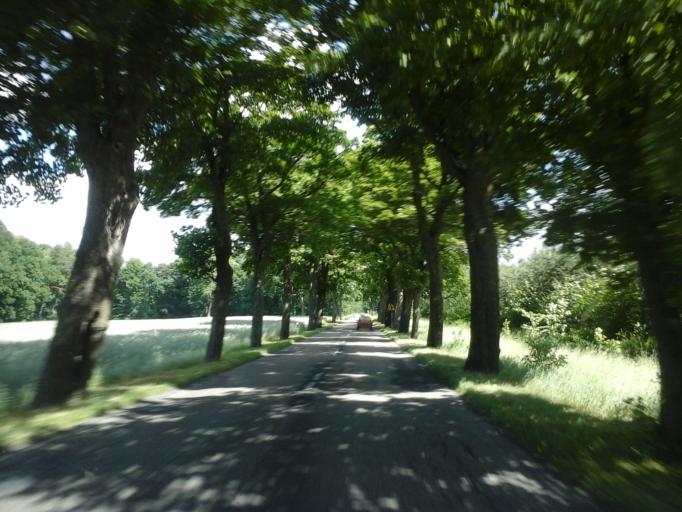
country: PL
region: West Pomeranian Voivodeship
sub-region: Powiat swidwinski
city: Swidwin
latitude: 53.7328
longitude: 15.7186
